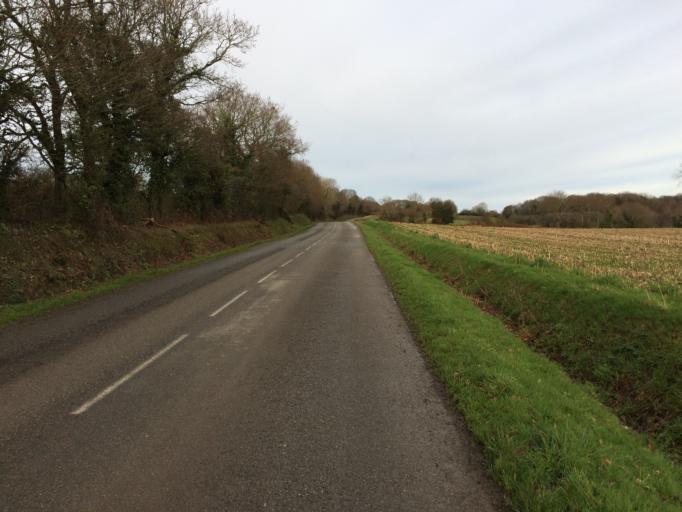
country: FR
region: Brittany
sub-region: Departement du Finistere
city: Daoulas
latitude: 48.3740
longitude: -4.2552
